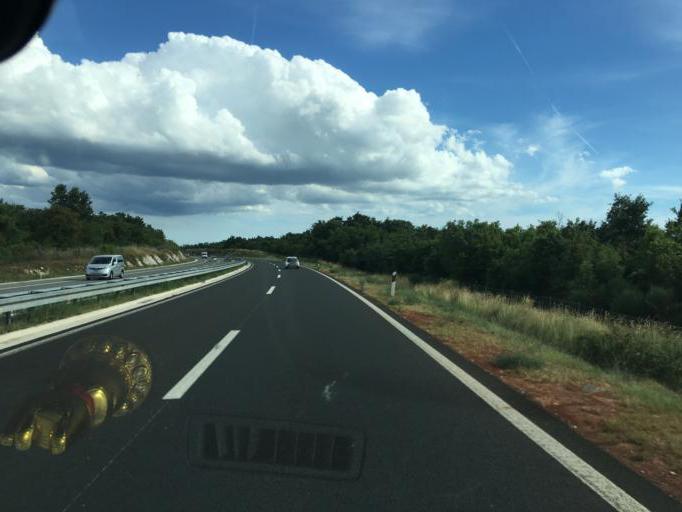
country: HR
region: Istarska
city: Vodnjan
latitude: 45.0359
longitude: 13.8306
